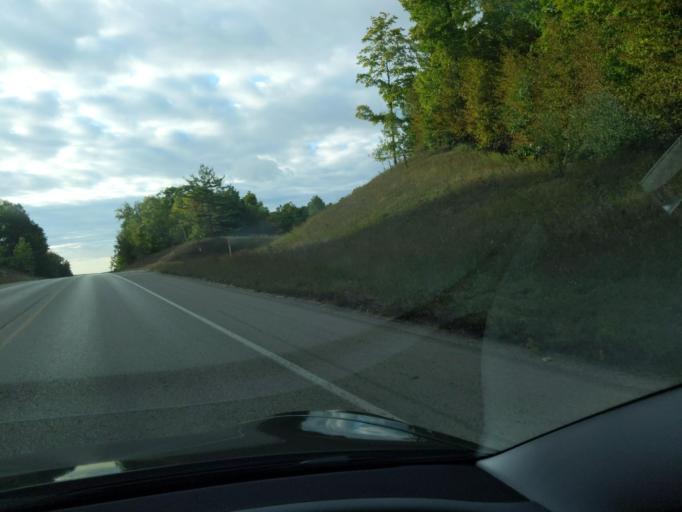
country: US
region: Michigan
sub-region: Kalkaska County
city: Rapid City
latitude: 44.7806
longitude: -85.2784
